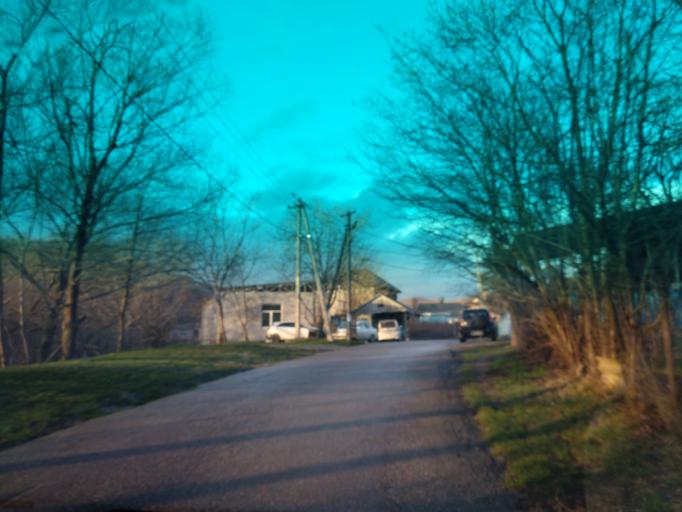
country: RU
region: Krasnodarskiy
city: Novomikhaylovskiy
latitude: 44.2728
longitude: 38.8328
